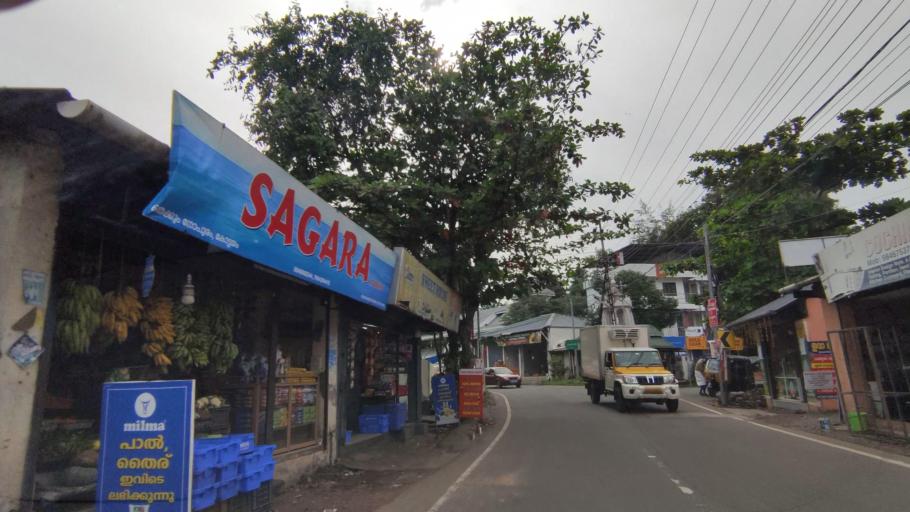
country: IN
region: Kerala
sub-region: Kottayam
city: Kottayam
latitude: 9.5877
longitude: 76.5181
